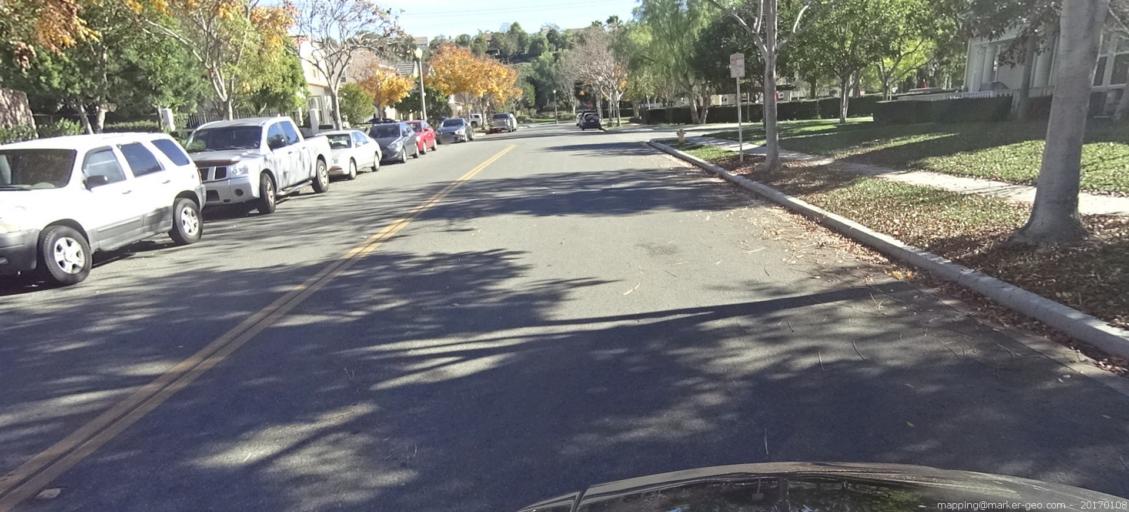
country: US
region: California
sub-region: Orange County
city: Ladera Ranch
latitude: 33.5527
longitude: -117.6448
